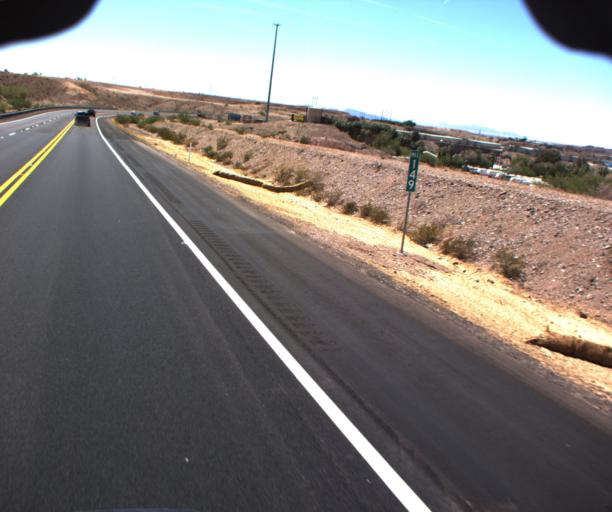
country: US
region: Arizona
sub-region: La Paz County
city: Cienega Springs
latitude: 34.1875
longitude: -114.2150
